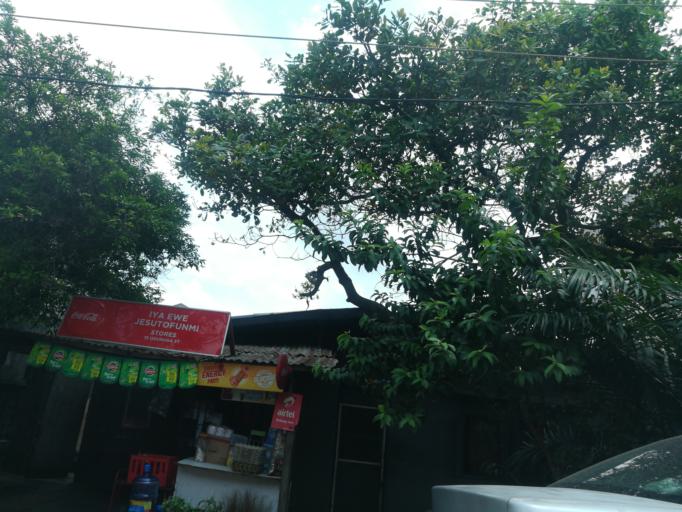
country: NG
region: Lagos
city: Ikeja
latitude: 6.5932
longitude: 3.3609
